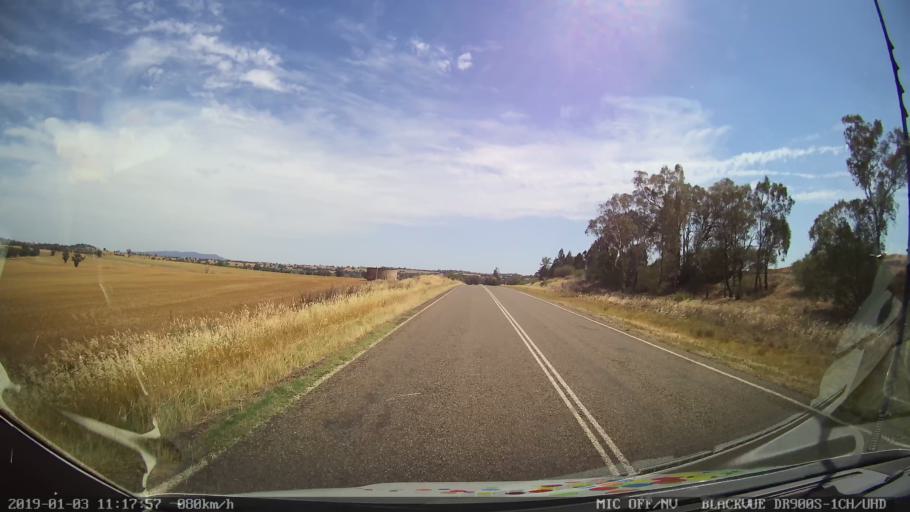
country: AU
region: New South Wales
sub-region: Young
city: Young
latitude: -34.1317
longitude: 148.2638
